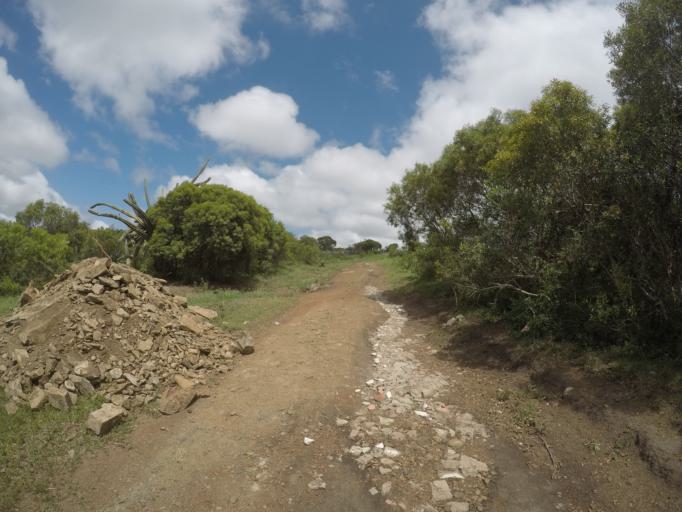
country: ZA
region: KwaZulu-Natal
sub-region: uThungulu District Municipality
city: Empangeni
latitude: -28.5734
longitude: 31.8294
